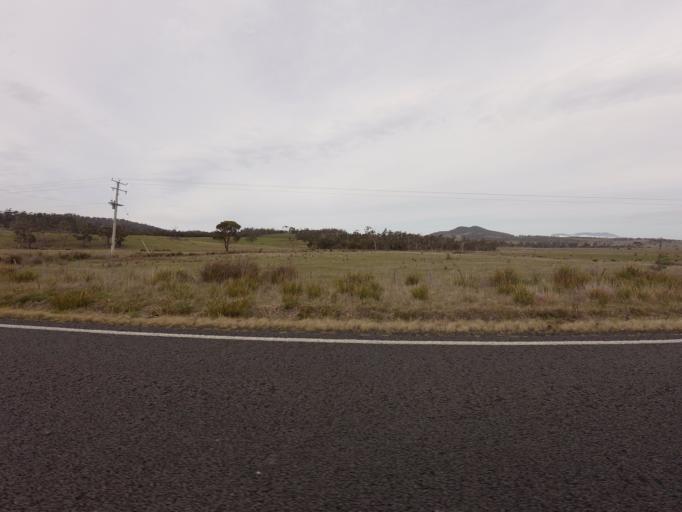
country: AU
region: Tasmania
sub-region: Sorell
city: Sorell
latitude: -42.4404
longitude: 147.9282
